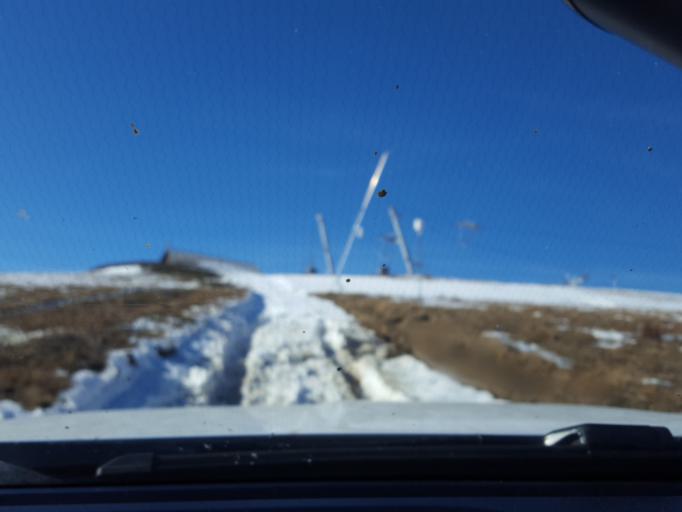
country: FR
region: Rhone-Alpes
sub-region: Departement de la Savoie
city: Saint-Jean-de-Maurienne
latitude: 45.2210
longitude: 6.2646
